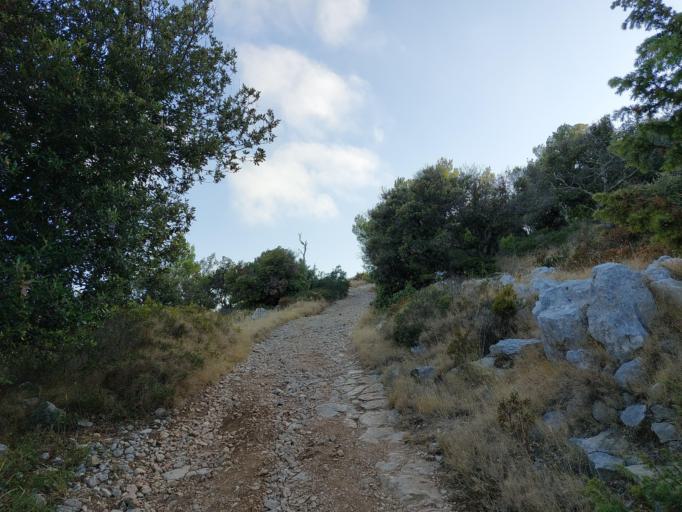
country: HR
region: Dubrovacko-Neretvanska
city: Smokvica
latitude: 42.7513
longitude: 16.8621
